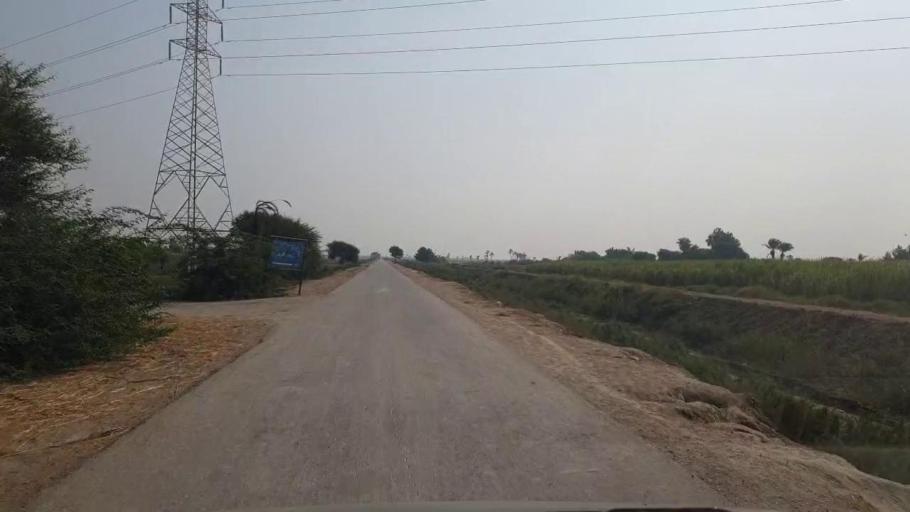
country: PK
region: Sindh
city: Tando Muhammad Khan
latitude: 25.1064
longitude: 68.3681
